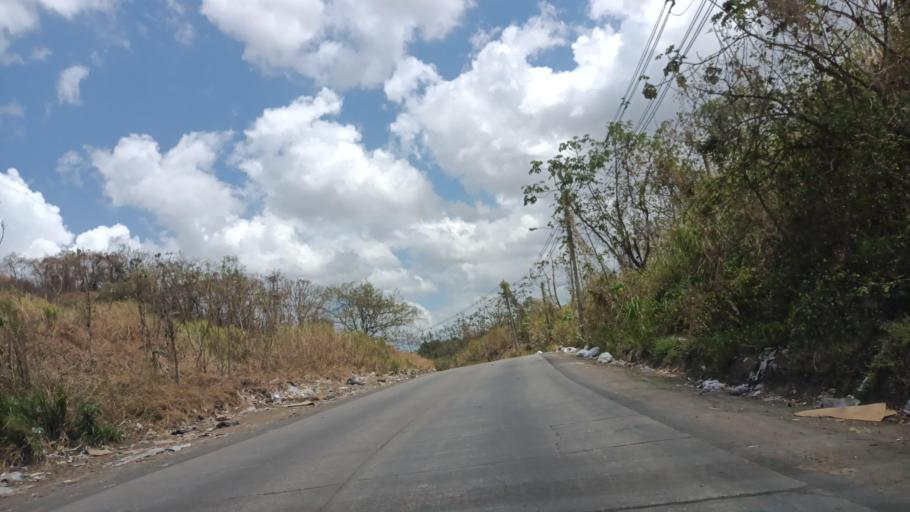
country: PA
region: Panama
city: Las Cumbres
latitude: 9.0512
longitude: -79.5629
